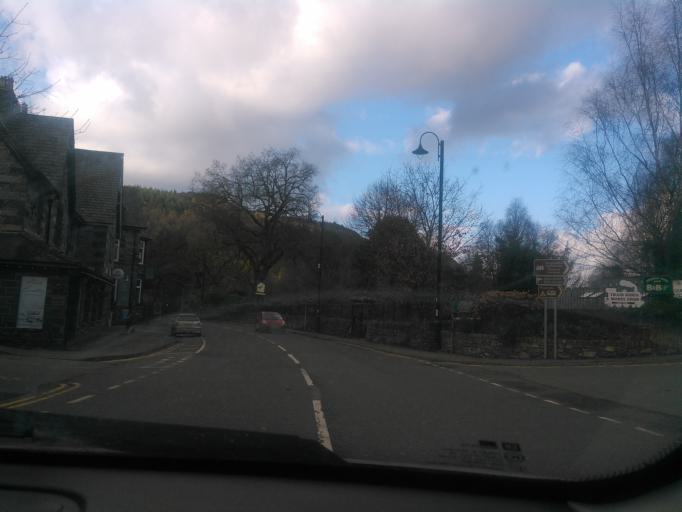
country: GB
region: Wales
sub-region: Conwy
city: Betws-y-Coed
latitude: 53.0904
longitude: -3.8004
